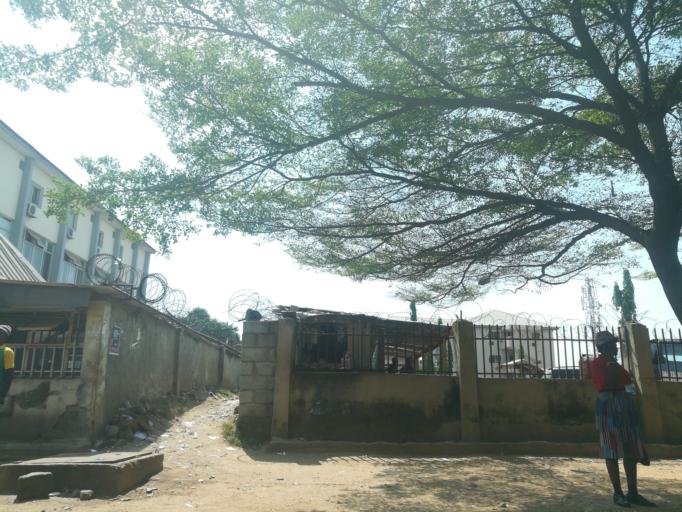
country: NG
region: Abuja Federal Capital Territory
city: Abuja
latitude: 9.0668
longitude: 7.4423
